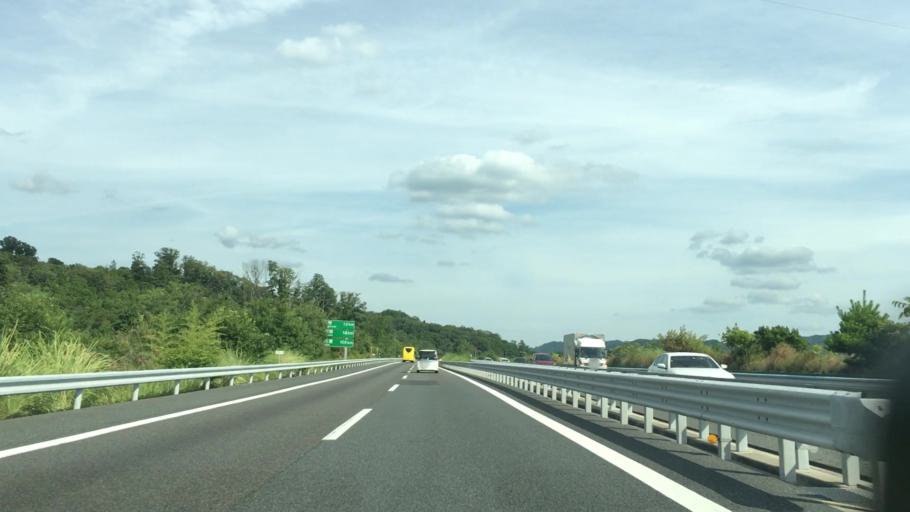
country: JP
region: Shiga Prefecture
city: Kusatsu
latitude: 34.9641
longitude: 135.9658
